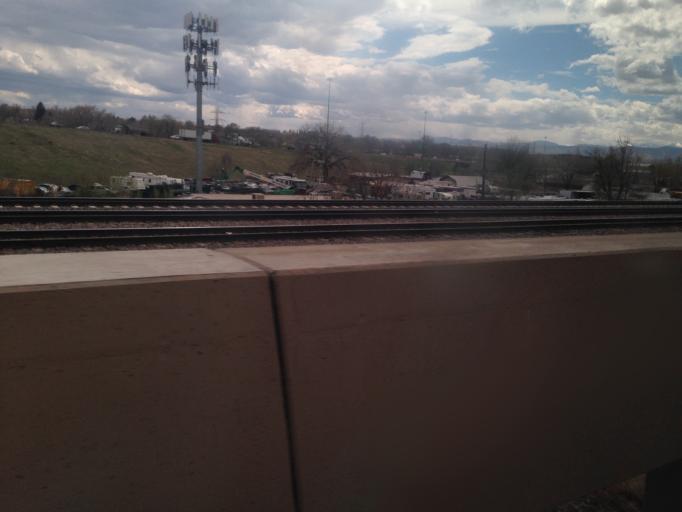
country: US
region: Colorado
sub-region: Adams County
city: Berkley
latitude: 39.8038
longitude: -105.0213
